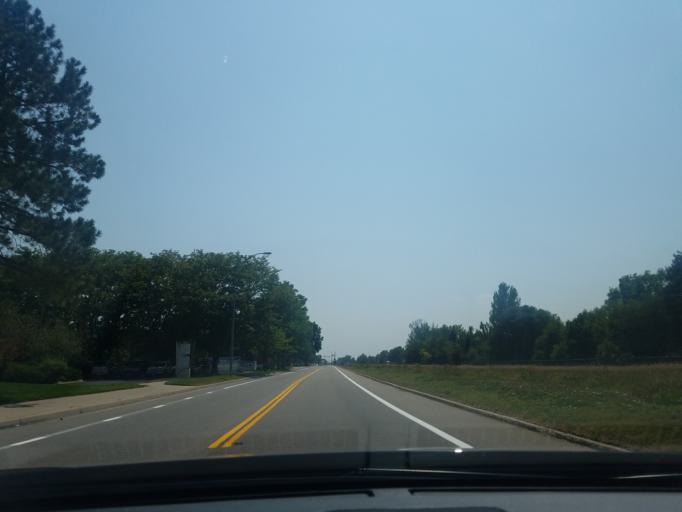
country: US
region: Colorado
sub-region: Larimer County
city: Fort Collins
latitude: 40.5489
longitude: -105.0798
